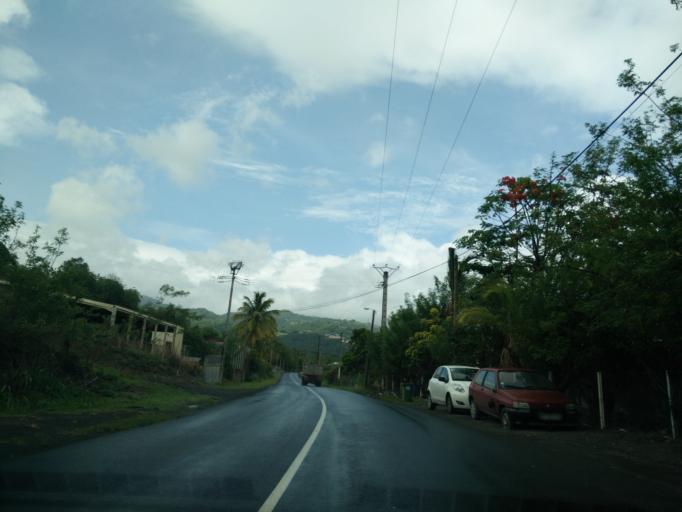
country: MQ
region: Martinique
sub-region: Martinique
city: Saint-Pierre
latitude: 14.7617
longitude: -61.1906
